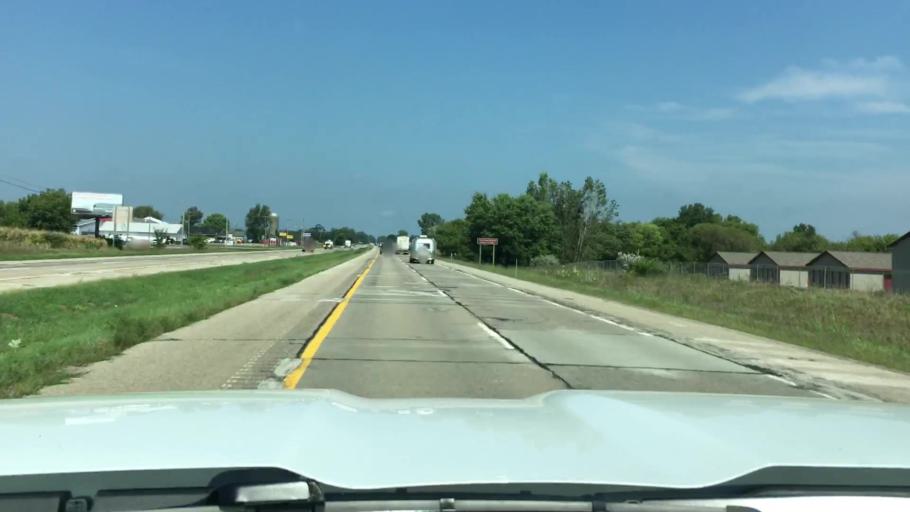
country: US
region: Michigan
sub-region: Kalamazoo County
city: Schoolcraft
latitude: 42.0939
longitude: -85.6367
